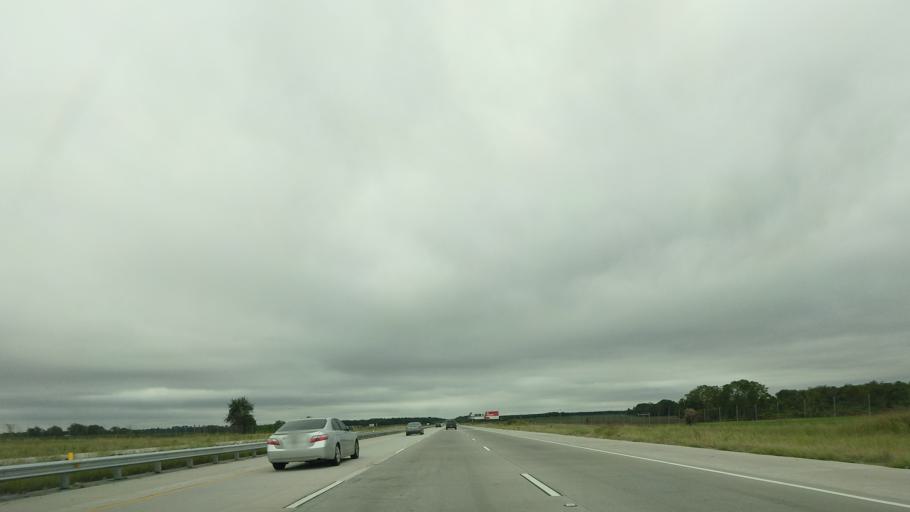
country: US
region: Georgia
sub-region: Dooly County
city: Vienna
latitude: 32.1565
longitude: -83.7553
